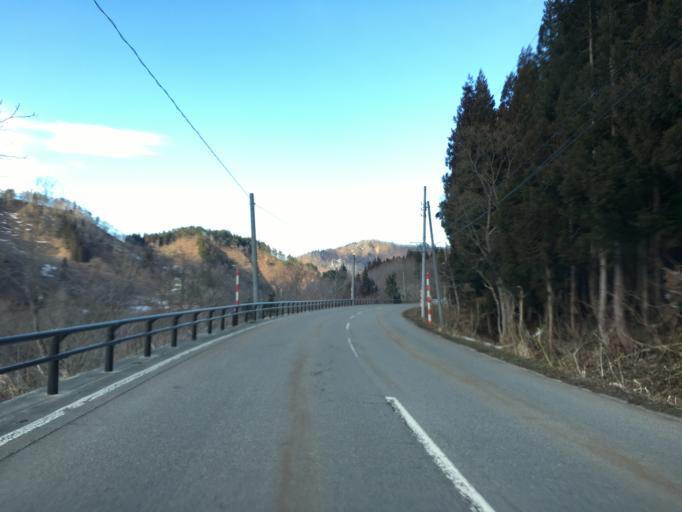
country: JP
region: Yamagata
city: Nagai
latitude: 37.9427
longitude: 139.9123
